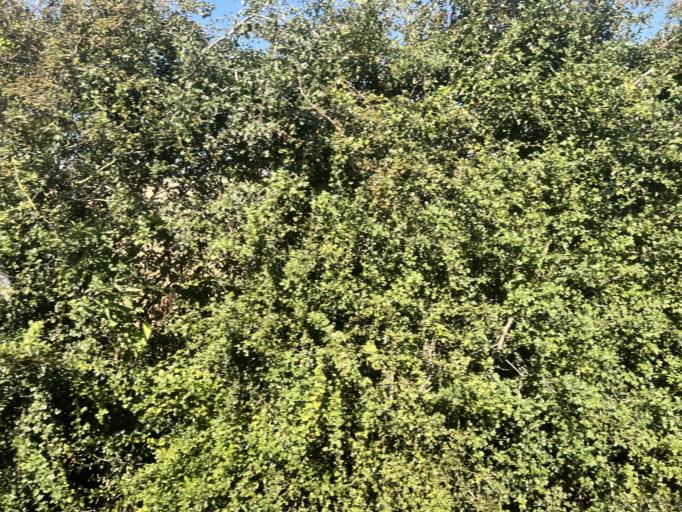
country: GB
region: England
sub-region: Lincolnshire
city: Spilsby
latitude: 53.0714
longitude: 0.0732
